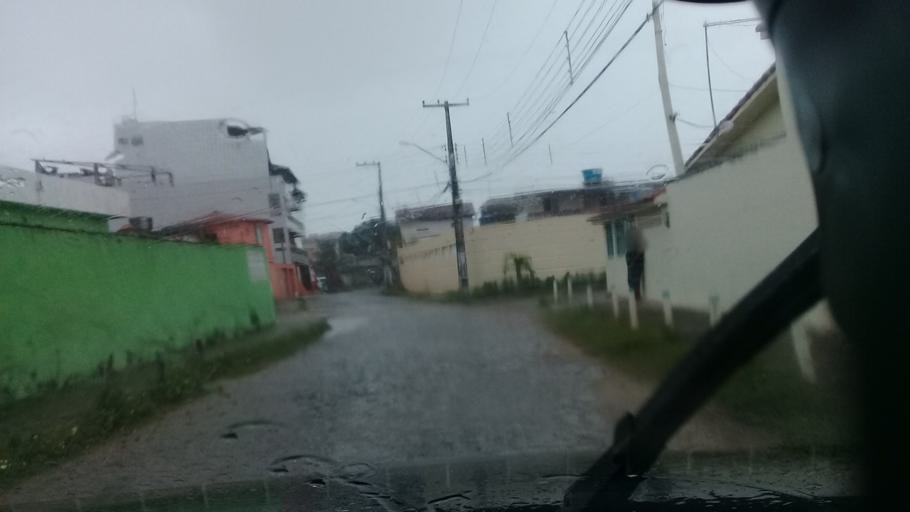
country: BR
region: Pernambuco
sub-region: Itamaraca
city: Itamaraca
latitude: -7.7437
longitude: -34.8254
